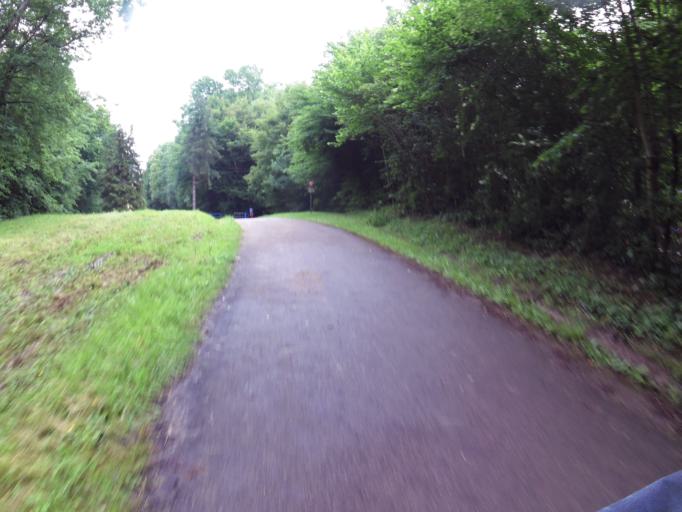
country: FR
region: Champagne-Ardenne
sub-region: Departement de la Haute-Marne
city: Villiers-en-Lieu
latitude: 48.5774
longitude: 4.8526
